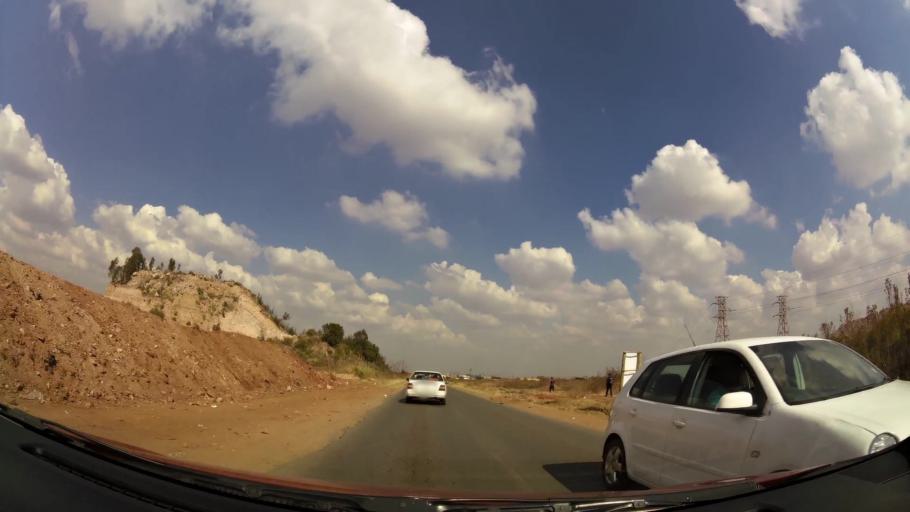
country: ZA
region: Gauteng
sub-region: City of Johannesburg Metropolitan Municipality
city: Roodepoort
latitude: -26.1854
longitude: 27.8687
